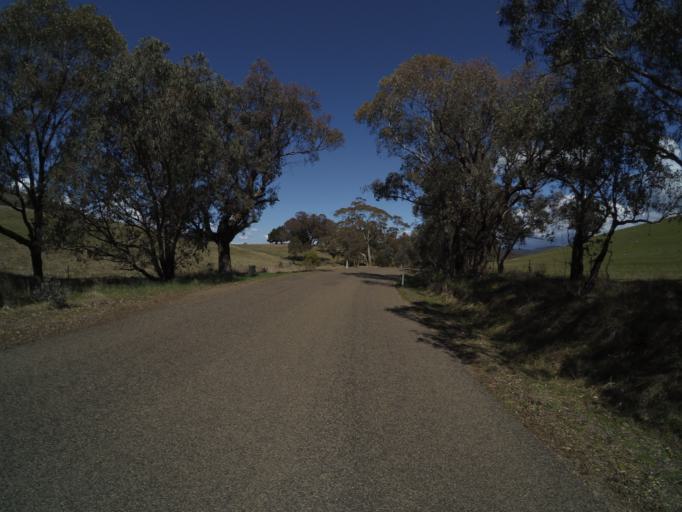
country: AU
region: Australian Capital Territory
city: Macquarie
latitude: -35.1843
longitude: 148.8911
